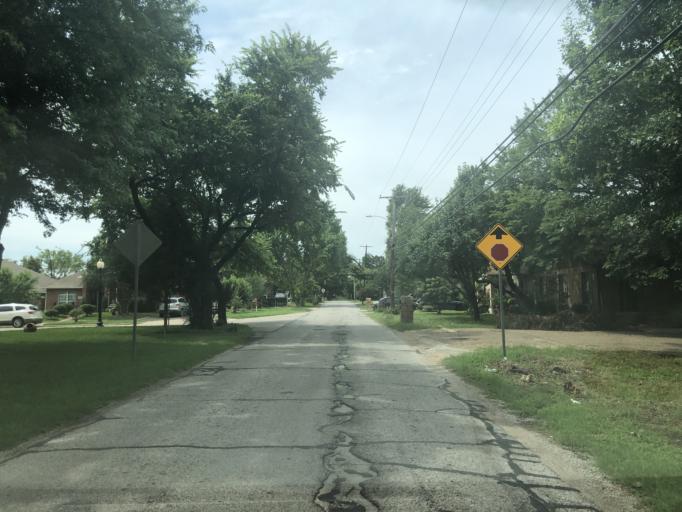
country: US
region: Texas
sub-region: Dallas County
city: Irving
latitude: 32.7953
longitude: -96.9803
